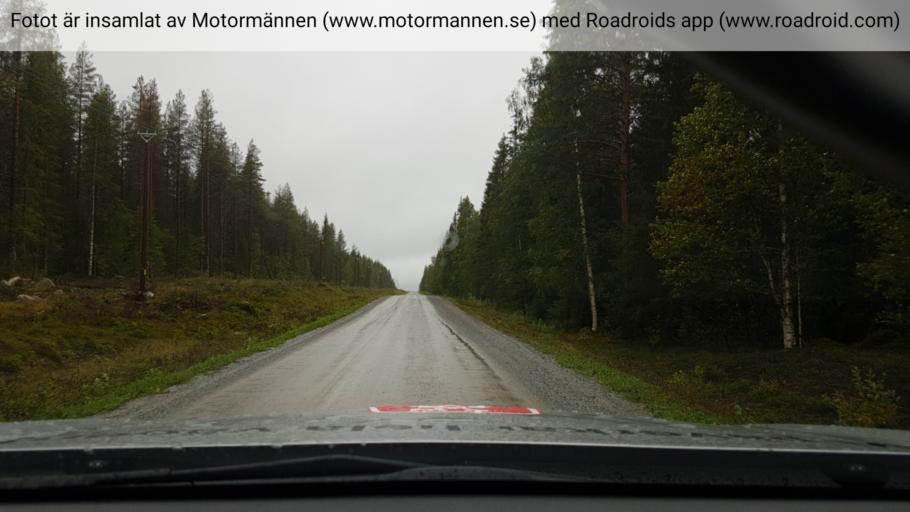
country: SE
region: Vaesterbotten
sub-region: Asele Kommun
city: Insjon
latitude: 64.0869
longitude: 17.7522
